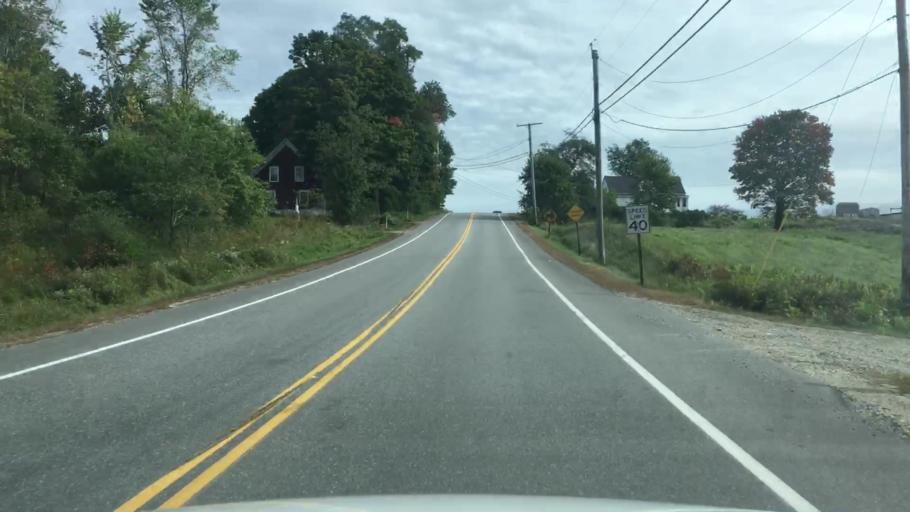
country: US
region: Maine
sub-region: Androscoggin County
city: Lisbon Falls
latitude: 43.9538
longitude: -70.0391
